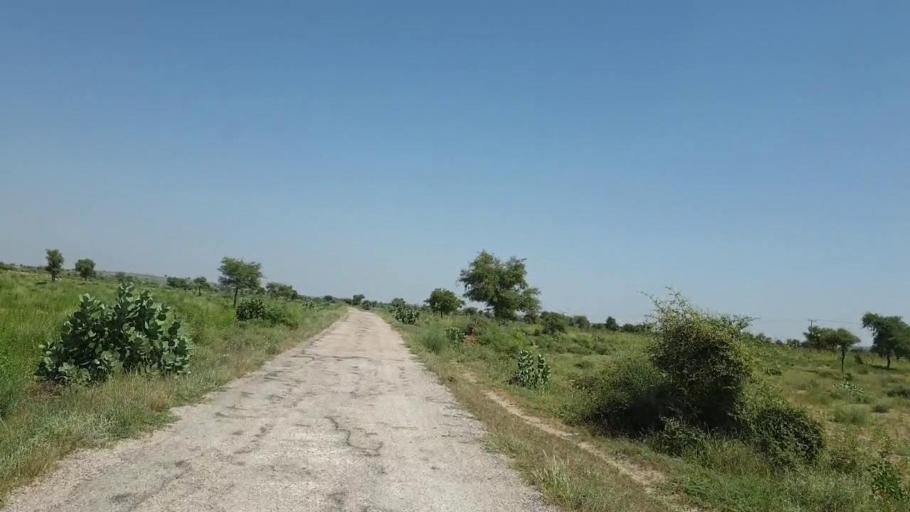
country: PK
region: Sindh
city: Islamkot
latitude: 25.1380
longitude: 70.3932
